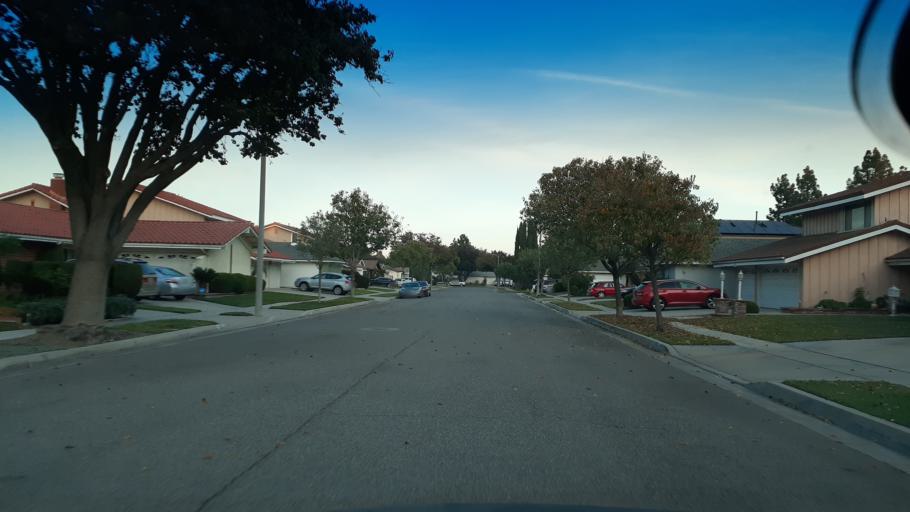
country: US
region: California
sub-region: Los Angeles County
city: Artesia
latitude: 33.8554
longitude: -118.0785
